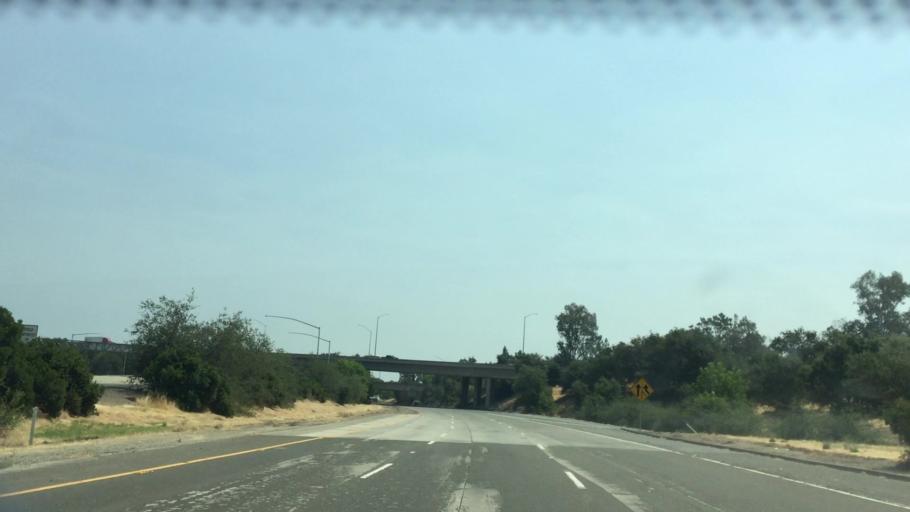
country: US
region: California
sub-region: Sacramento County
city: North Highlands
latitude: 38.6450
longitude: -121.3804
